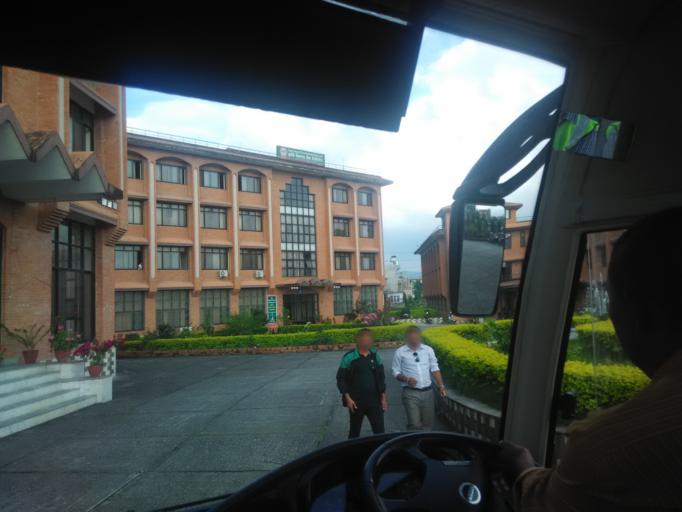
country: NP
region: Central Region
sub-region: Bagmati Zone
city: Bhaktapur
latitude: 27.6895
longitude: 85.3961
